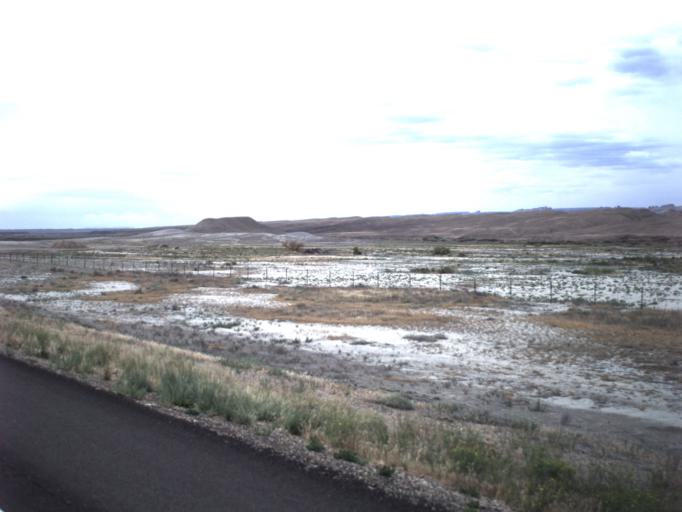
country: US
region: Utah
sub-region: Carbon County
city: East Carbon City
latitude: 39.0747
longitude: -110.3164
